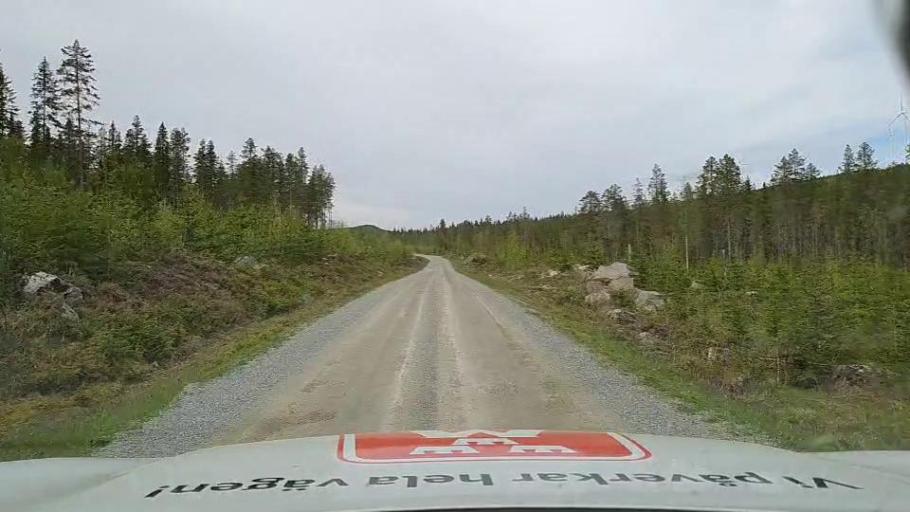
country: SE
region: Jaemtland
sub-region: Bergs Kommun
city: Hoverberg
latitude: 62.5481
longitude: 14.8979
